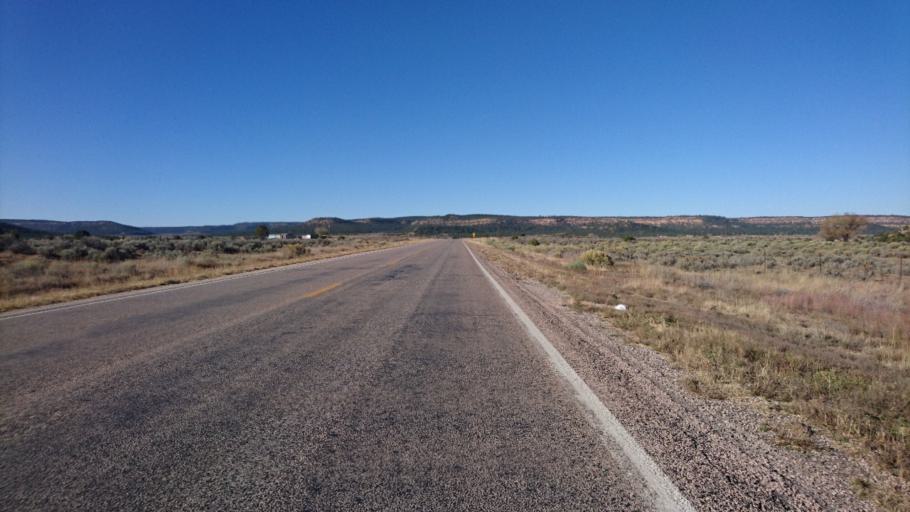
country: US
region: New Mexico
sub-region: McKinley County
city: Black Rock
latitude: 35.1082
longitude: -108.5645
